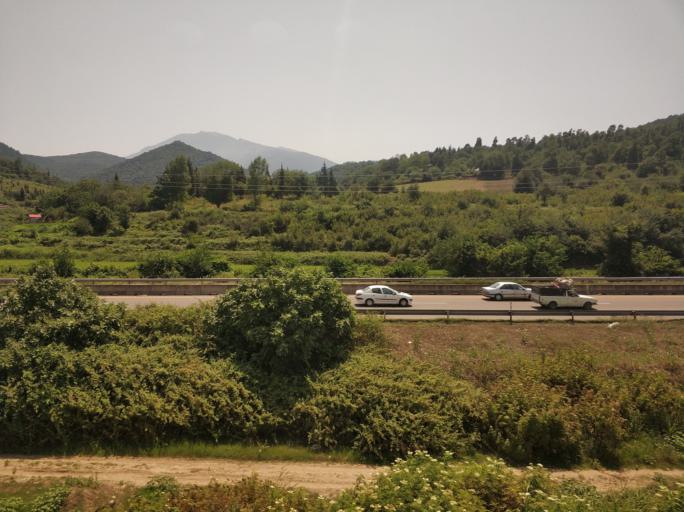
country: IR
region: Gilan
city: Pa'in-e Bazar-e Rudbar
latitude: 36.9399
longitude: 49.5469
